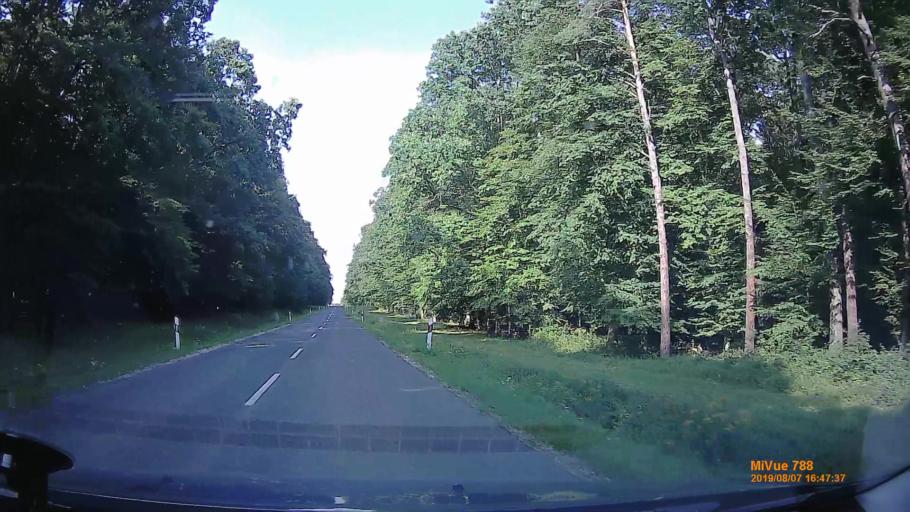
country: HU
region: Zala
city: Lenti
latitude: 46.6641
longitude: 16.6372
